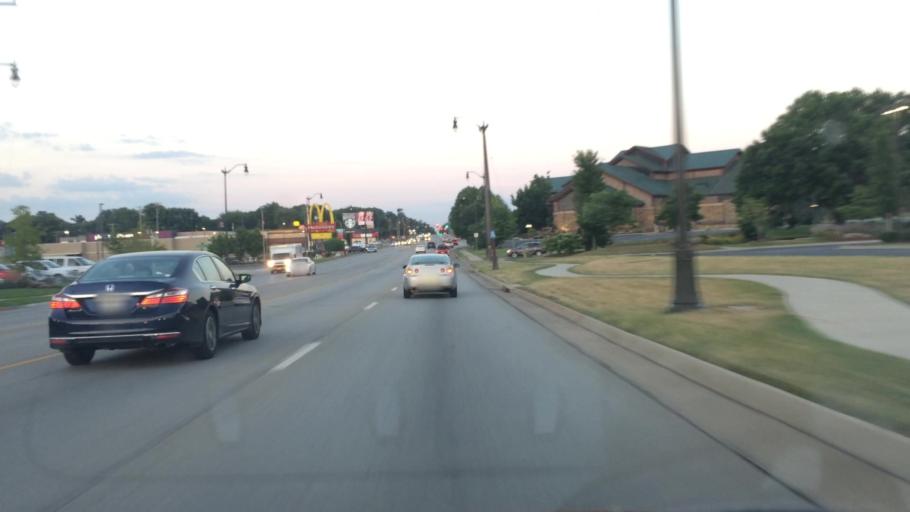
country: US
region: Missouri
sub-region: Greene County
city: Springfield
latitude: 37.1822
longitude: -93.2988
